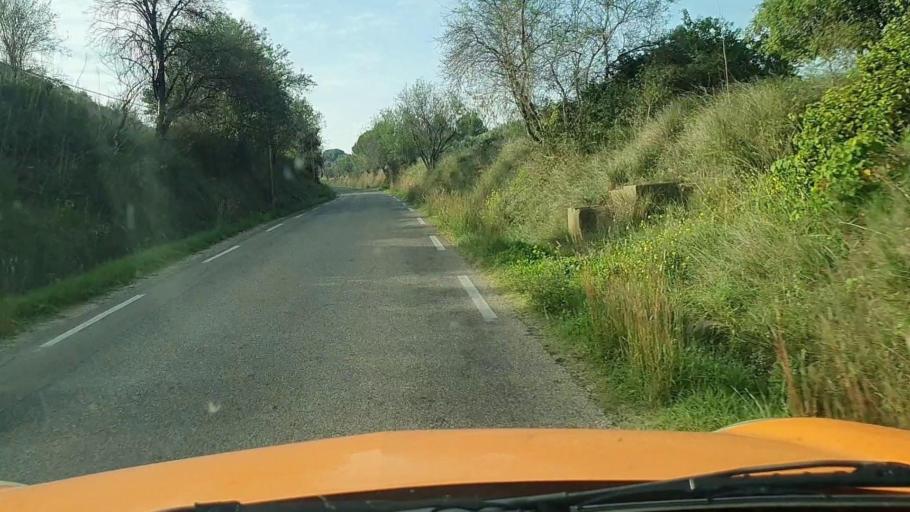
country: FR
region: Languedoc-Roussillon
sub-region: Departement du Gard
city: Generac
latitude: 43.7196
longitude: 4.3410
